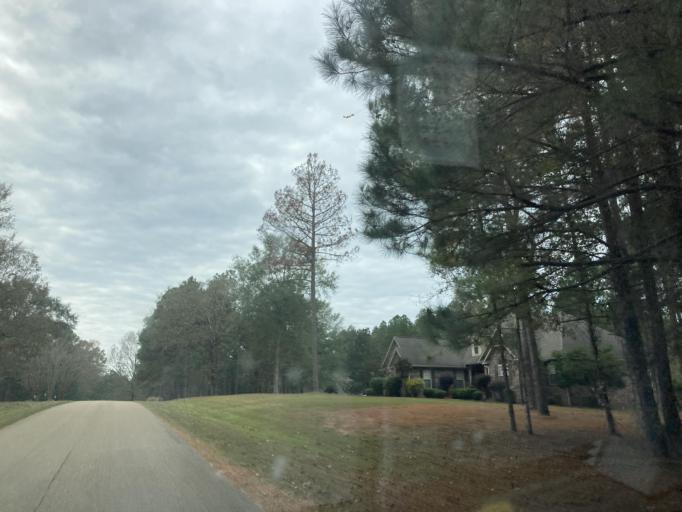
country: US
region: Mississippi
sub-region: Lamar County
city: West Hattiesburg
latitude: 31.3021
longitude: -89.4467
